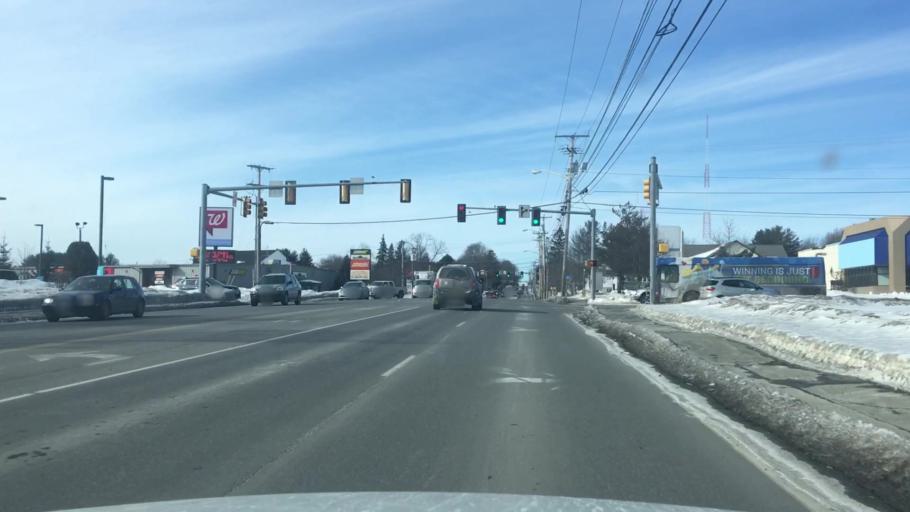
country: US
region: Maine
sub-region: Penobscot County
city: Bangor
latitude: 44.8243
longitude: -68.7801
